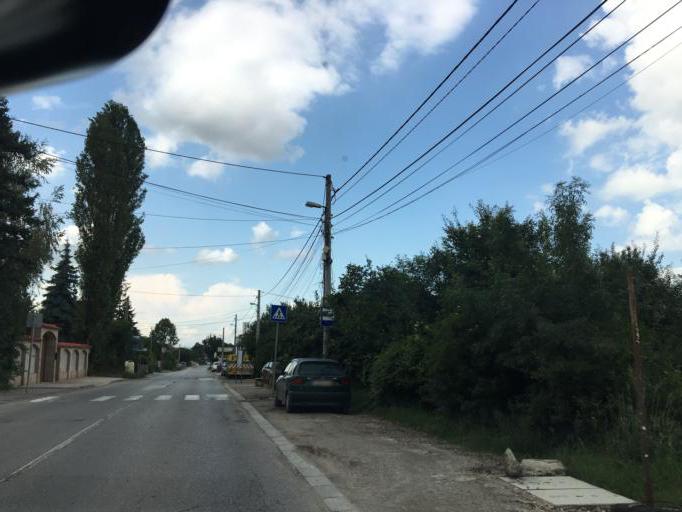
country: BG
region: Sofia-Capital
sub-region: Stolichna Obshtina
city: Sofia
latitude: 42.6346
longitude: 23.3540
